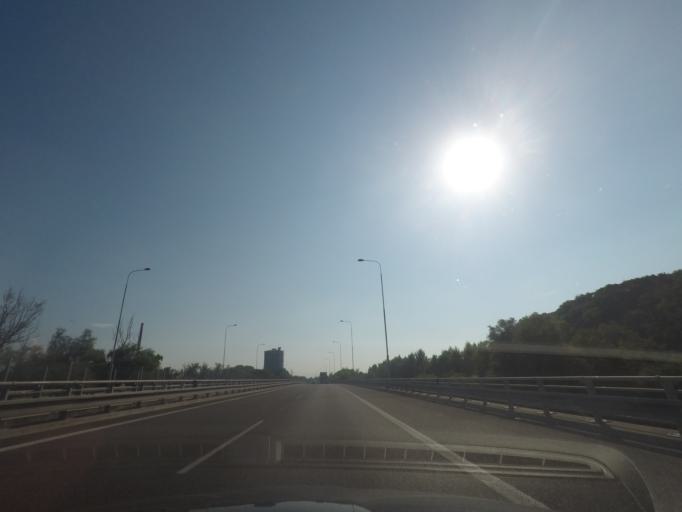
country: CZ
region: Moravskoslezsky
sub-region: Okres Ostrava-Mesto
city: Ostrava
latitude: 49.8686
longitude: 18.2817
